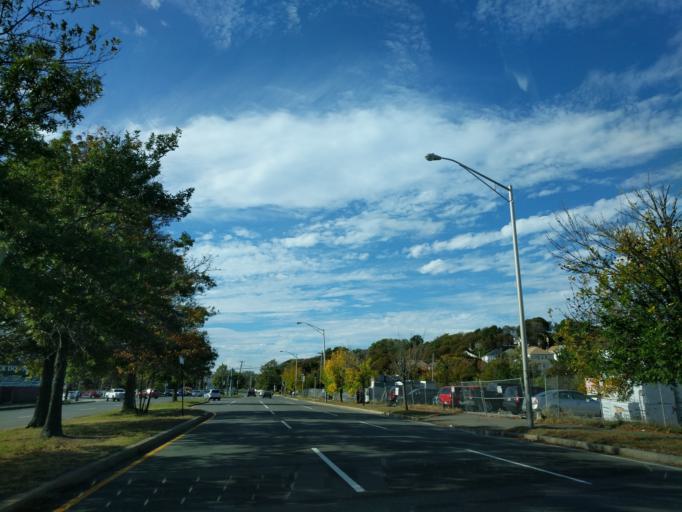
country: US
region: Massachusetts
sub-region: Suffolk County
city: Revere
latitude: 42.4000
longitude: -70.9958
